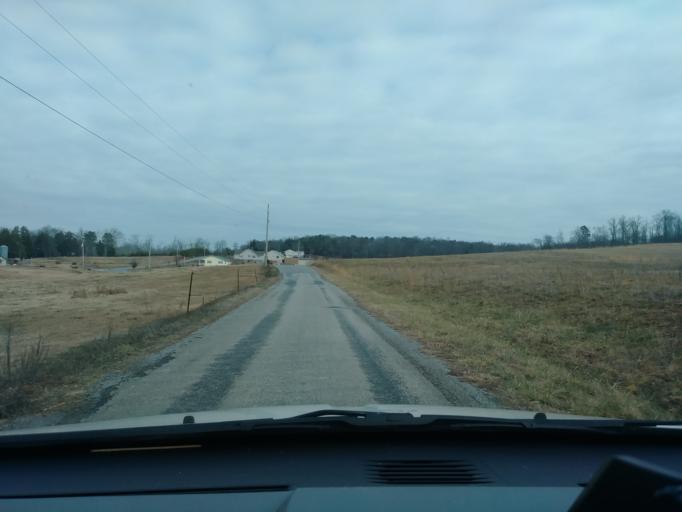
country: US
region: Tennessee
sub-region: Greene County
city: Mosheim
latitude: 36.0971
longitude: -82.9127
